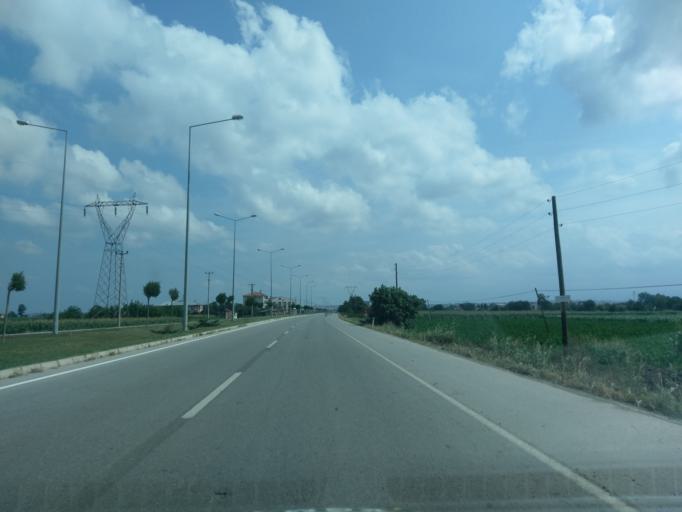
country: TR
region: Samsun
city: Bafra
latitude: 41.5776
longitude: 35.8529
